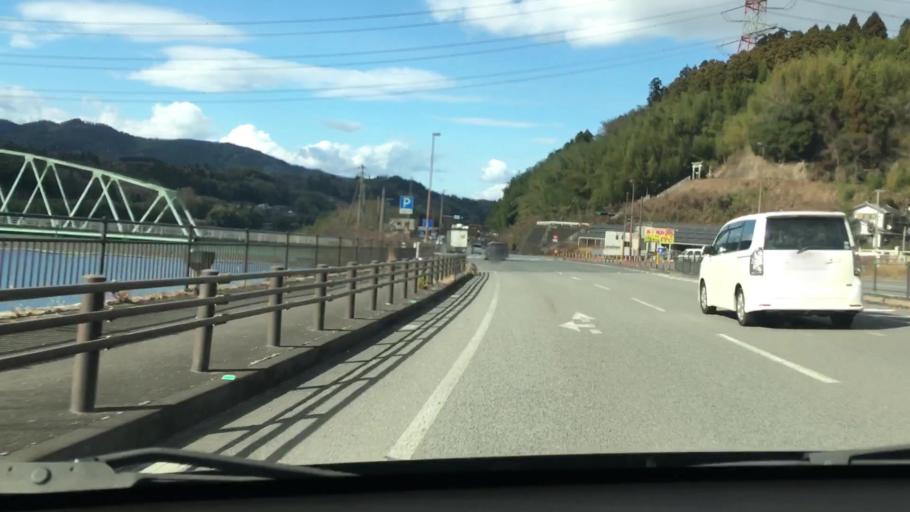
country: JP
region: Oita
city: Oita
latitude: 33.1121
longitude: 131.6564
